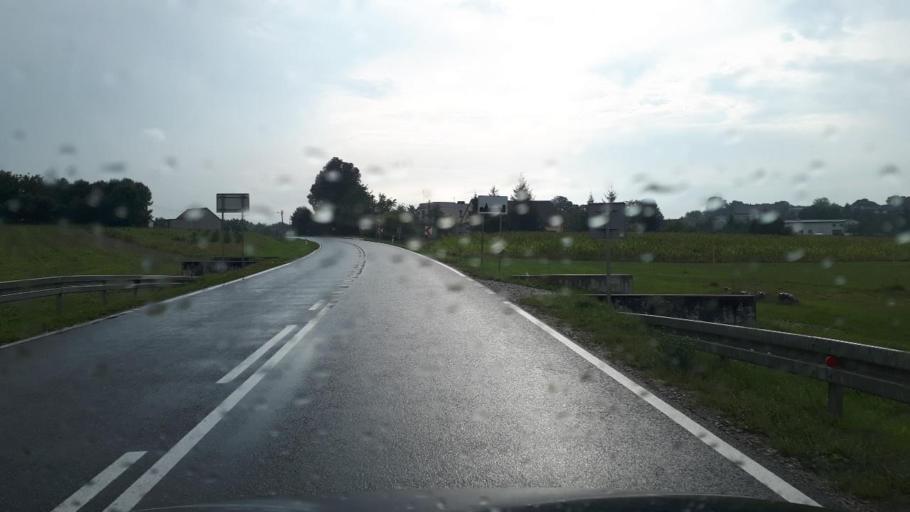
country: PL
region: Silesian Voivodeship
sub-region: Powiat gliwicki
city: Wielowies
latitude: 50.4965
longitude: 18.5926
